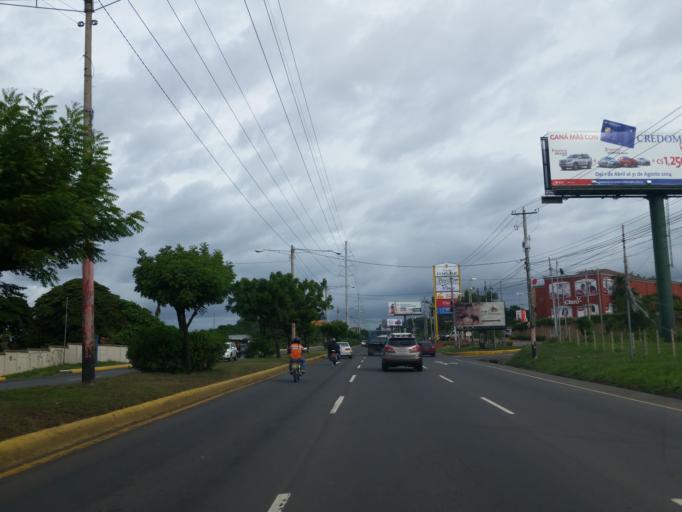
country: NI
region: Managua
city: Managua
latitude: 12.1030
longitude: -86.2460
